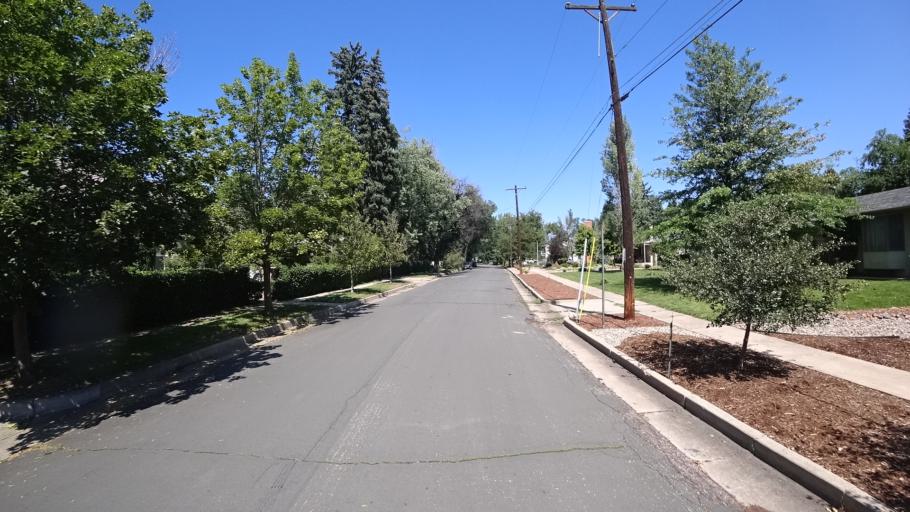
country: US
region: Colorado
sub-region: El Paso County
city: Colorado Springs
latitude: 38.8543
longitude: -104.8287
